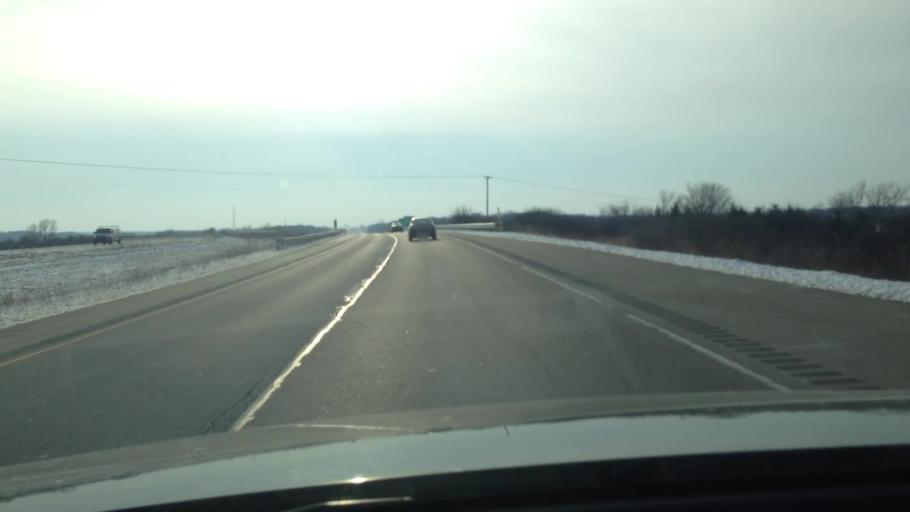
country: US
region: Wisconsin
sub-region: Walworth County
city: Elkhorn
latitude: 42.6933
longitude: -88.5025
